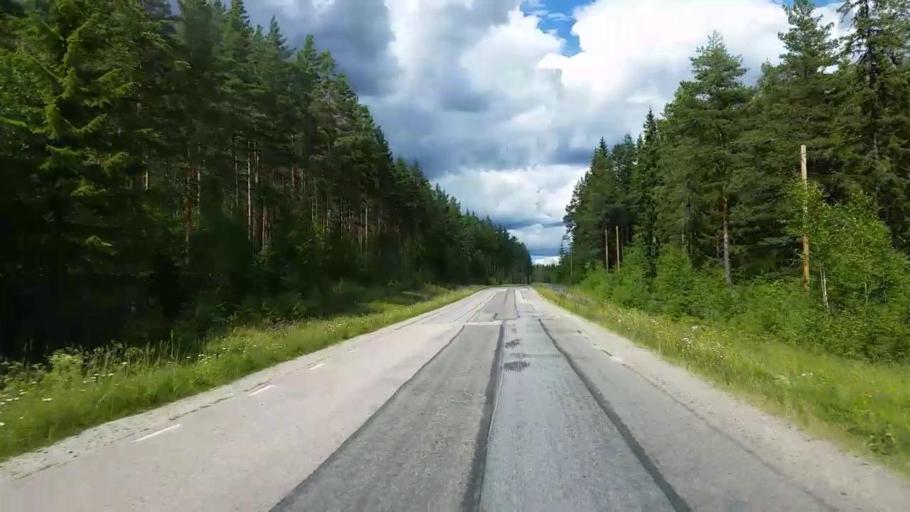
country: SE
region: Gaevleborg
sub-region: Ovanakers Kommun
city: Edsbyn
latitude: 61.4002
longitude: 15.8963
